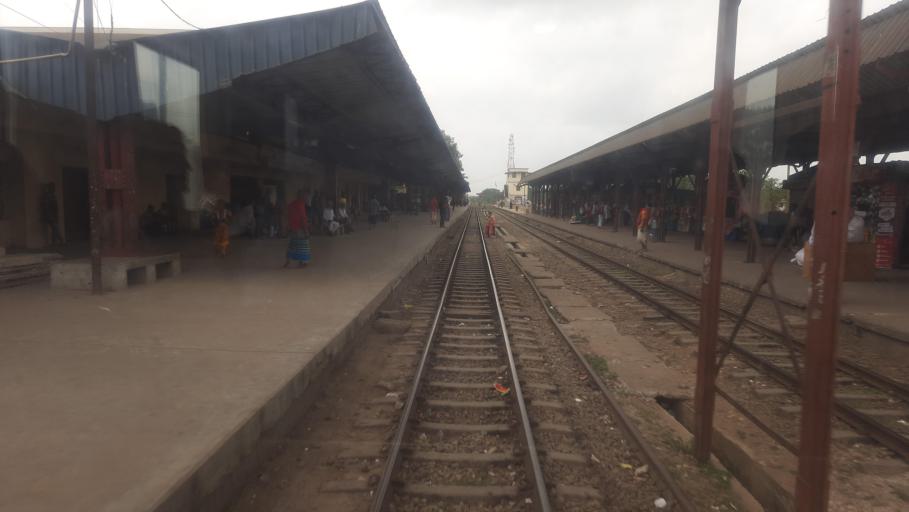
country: BD
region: Dhaka
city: Bhairab Bazar
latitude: 24.0504
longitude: 90.9784
